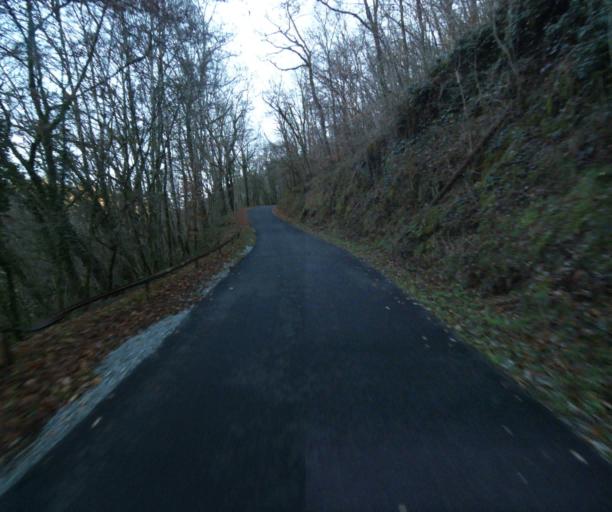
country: FR
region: Limousin
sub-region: Departement de la Correze
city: Laguenne
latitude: 45.2378
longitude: 1.7978
